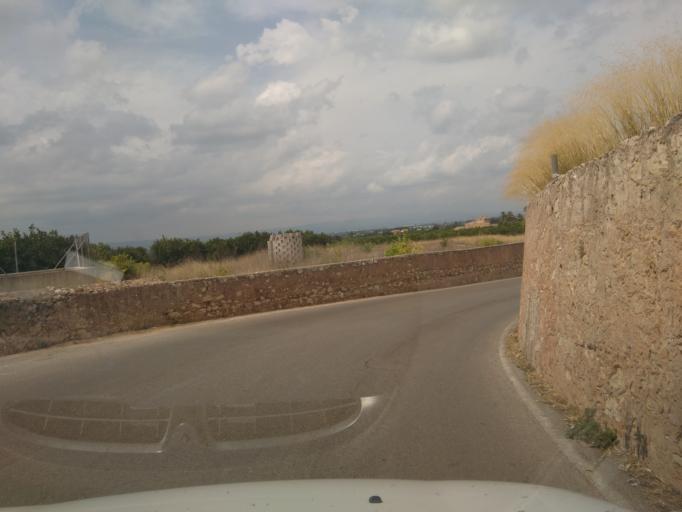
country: ES
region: Valencia
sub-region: Provincia de Valencia
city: La Pobla Llarga
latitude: 39.0969
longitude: -0.4316
